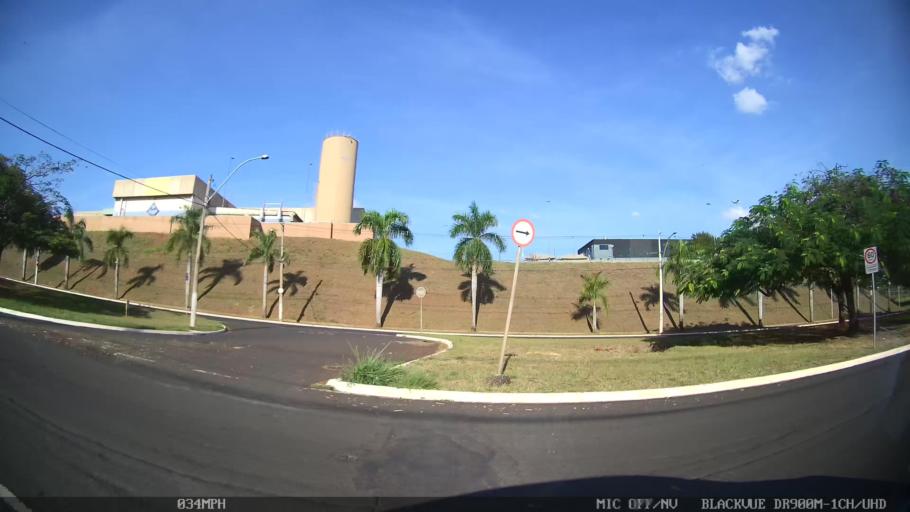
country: BR
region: Sao Paulo
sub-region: Ribeirao Preto
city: Ribeirao Preto
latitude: -21.2090
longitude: -47.7709
